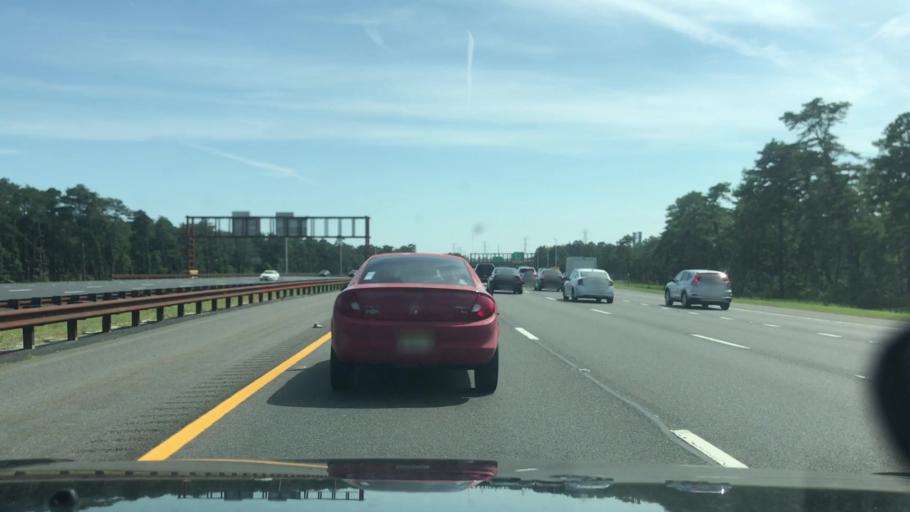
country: US
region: New Jersey
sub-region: Ocean County
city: Leisure Village
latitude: 40.0705
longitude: -74.1586
